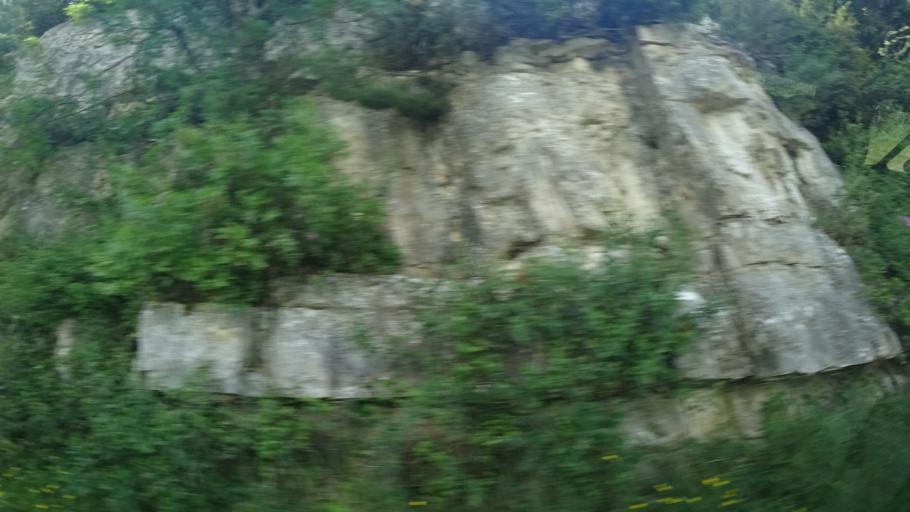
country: FR
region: Languedoc-Roussillon
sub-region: Departement de l'Herault
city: Olonzac
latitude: 43.3526
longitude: 2.7614
